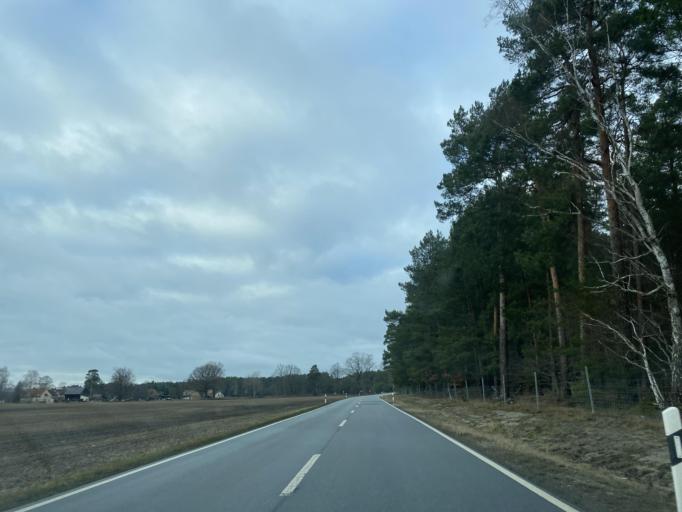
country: PL
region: Lubusz
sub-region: Powiat zarski
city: Leknica
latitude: 51.5101
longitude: 14.7792
